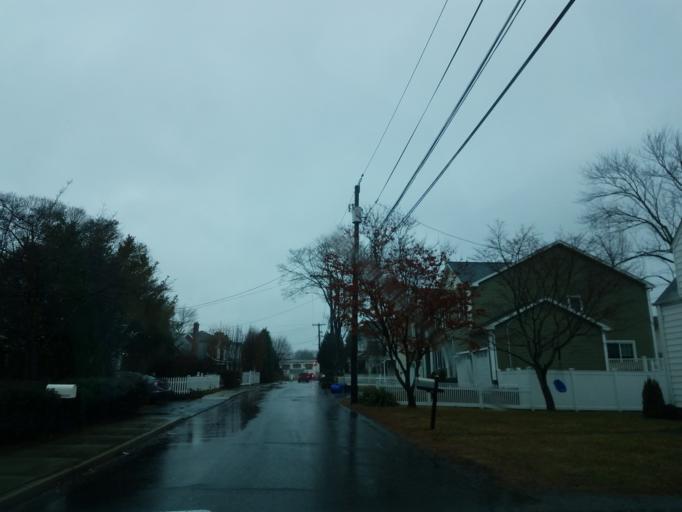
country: US
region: Connecticut
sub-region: Fairfield County
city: Southport
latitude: 41.1371
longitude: -73.2919
